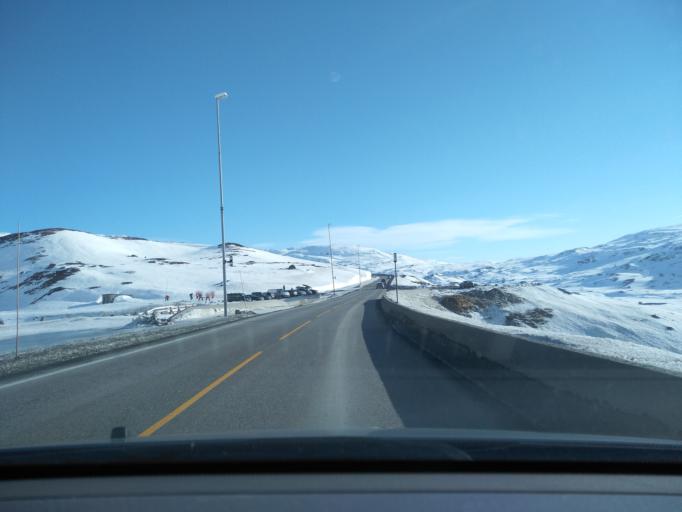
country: NO
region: Aust-Agder
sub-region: Bykle
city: Hovden
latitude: 59.8451
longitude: 6.9721
